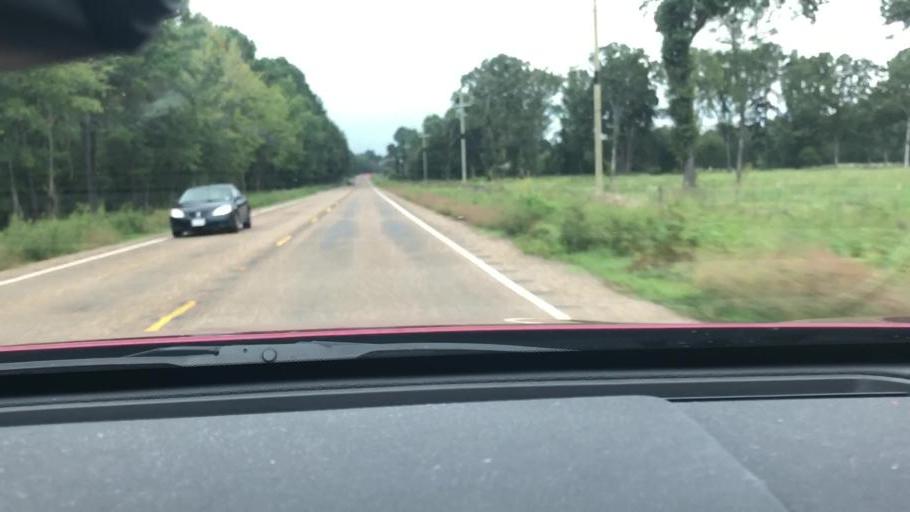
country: US
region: Texas
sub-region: Bowie County
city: Wake Village
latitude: 33.3774
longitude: -94.1010
